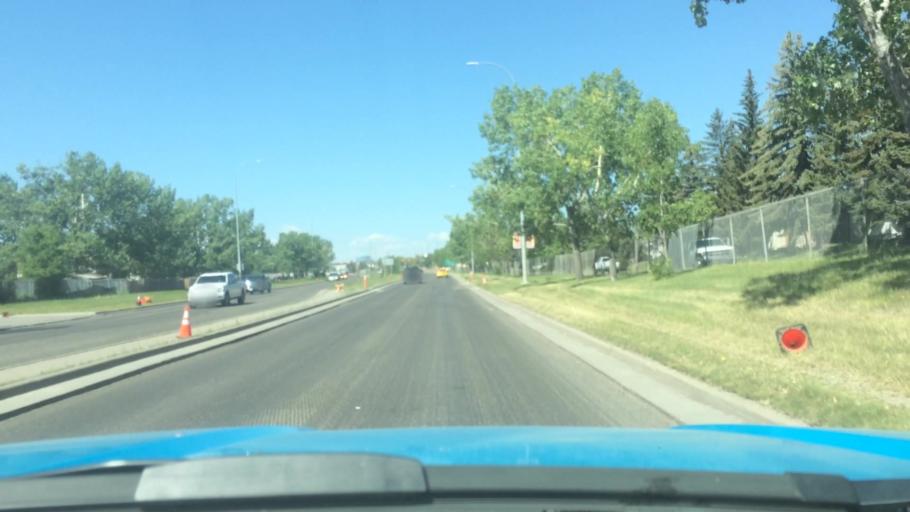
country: CA
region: Alberta
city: Calgary
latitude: 51.0529
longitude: -113.9709
